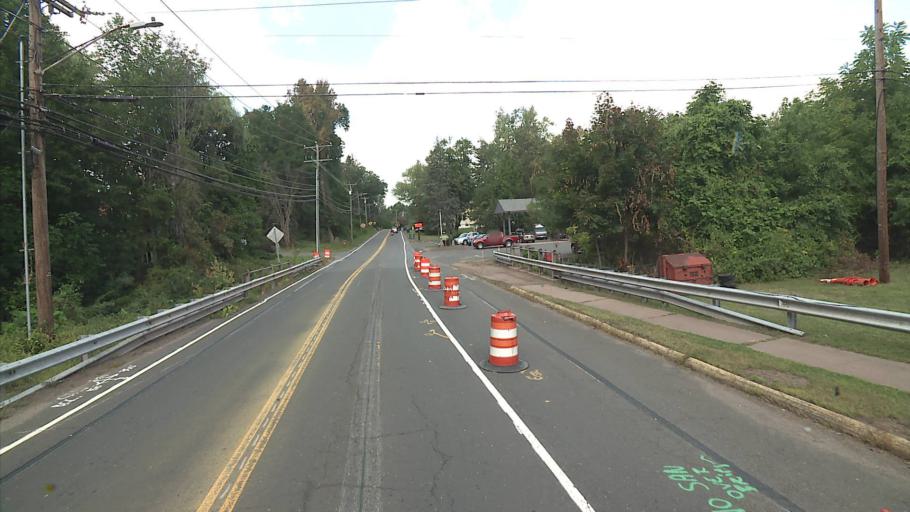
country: US
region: Connecticut
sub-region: Hartford County
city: Blue Hills
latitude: 41.8363
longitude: -72.7387
